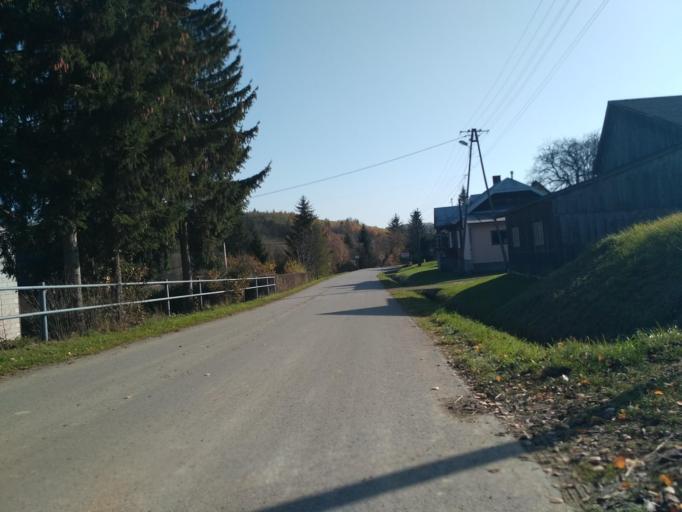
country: PL
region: Subcarpathian Voivodeship
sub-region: Powiat brzozowski
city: Nozdrzec
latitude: 49.8023
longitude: 22.1712
